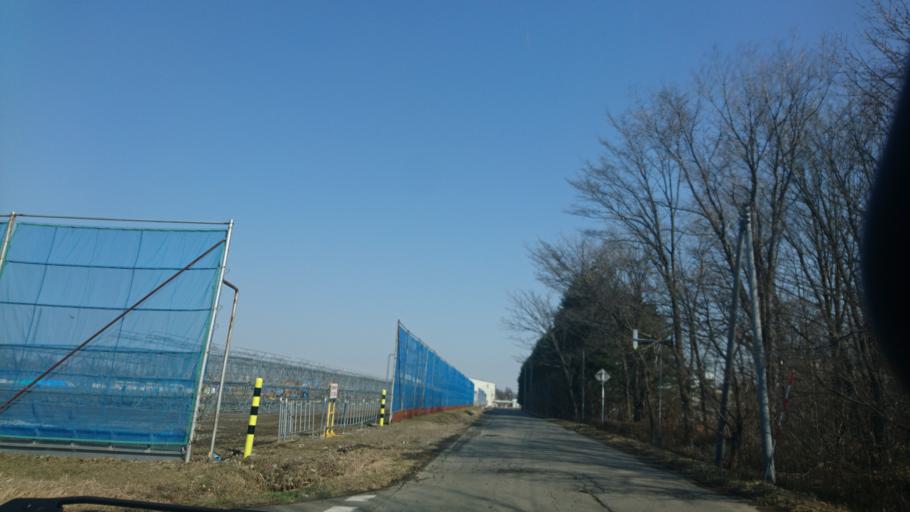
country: JP
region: Hokkaido
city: Obihiro
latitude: 42.9179
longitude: 143.0762
